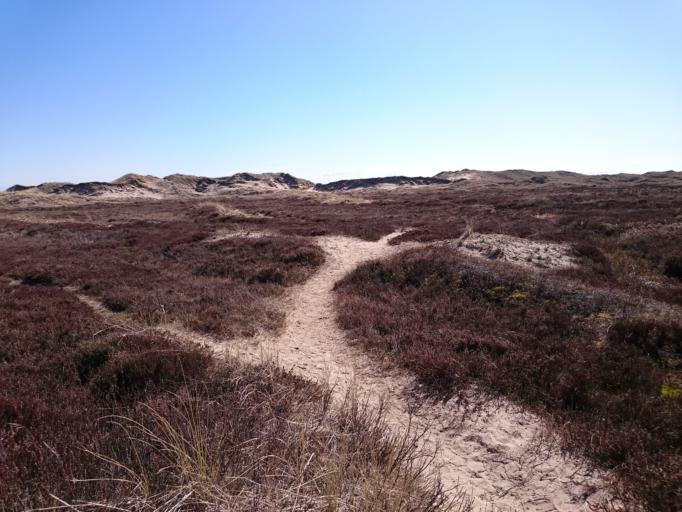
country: DK
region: North Denmark
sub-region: Frederikshavn Kommune
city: Skagen
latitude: 57.6954
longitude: 10.5241
